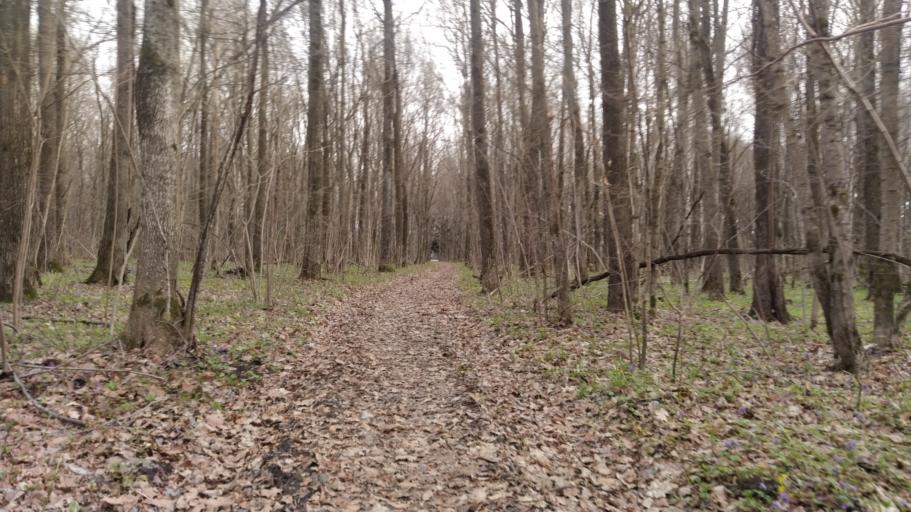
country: RU
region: Chuvashia
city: Novyye Lapsary
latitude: 56.1298
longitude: 47.1219
